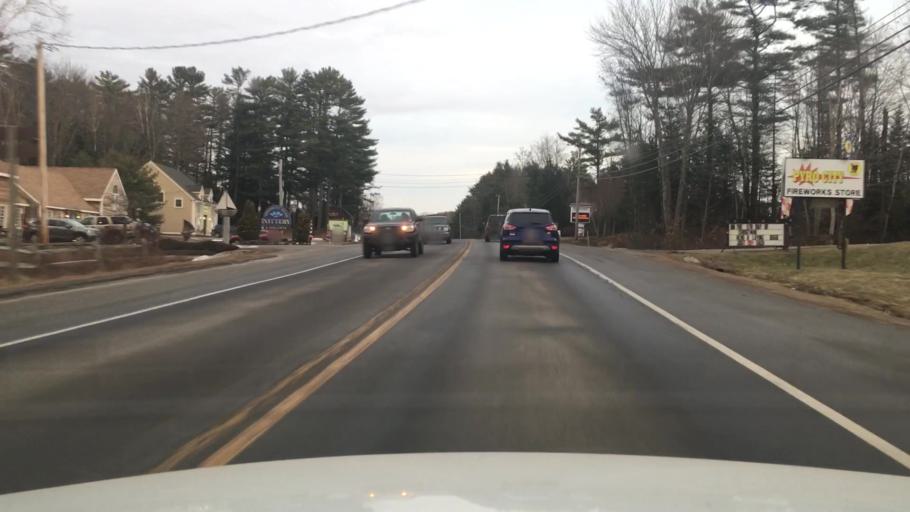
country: US
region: Maine
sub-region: Lincoln County
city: Wiscasset
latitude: 43.9997
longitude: -69.6500
